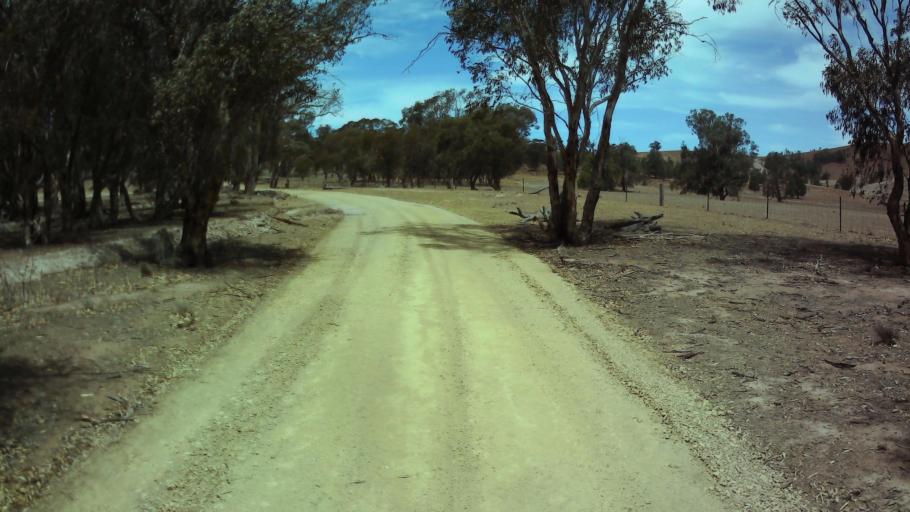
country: AU
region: New South Wales
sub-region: Weddin
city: Grenfell
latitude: -33.7849
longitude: 148.1525
